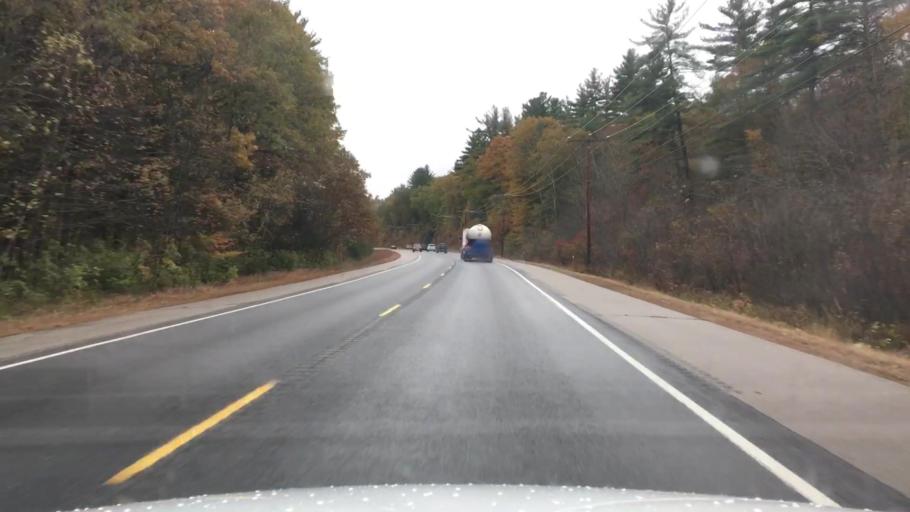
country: US
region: New Hampshire
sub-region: Strafford County
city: Lee
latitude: 43.1708
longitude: -71.0042
